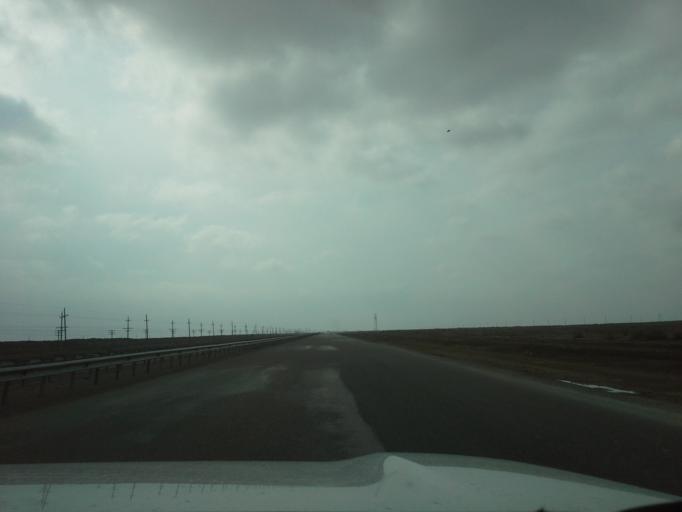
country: IR
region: Razavi Khorasan
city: Kalat-e Naderi
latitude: 37.2091
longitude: 60.0672
